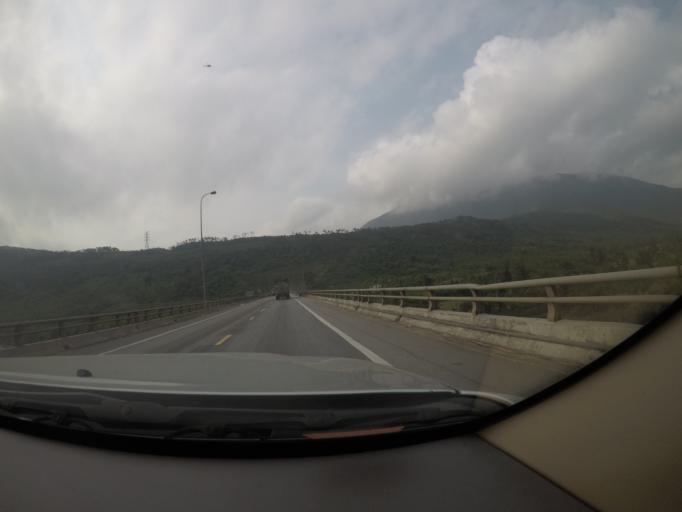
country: VN
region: Ha Tinh
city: Ky Anh
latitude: 17.9614
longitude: 106.4677
